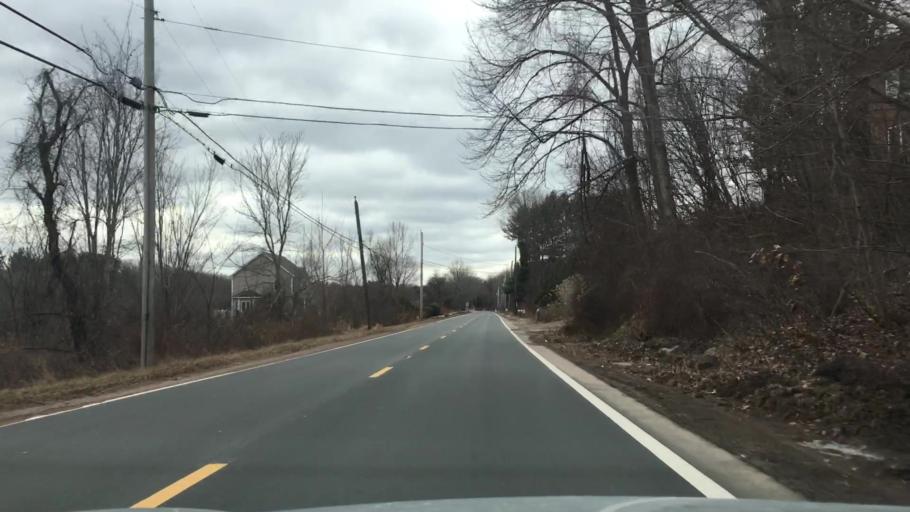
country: US
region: Connecticut
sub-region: Hartford County
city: North Granby
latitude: 42.0088
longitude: -72.7953
